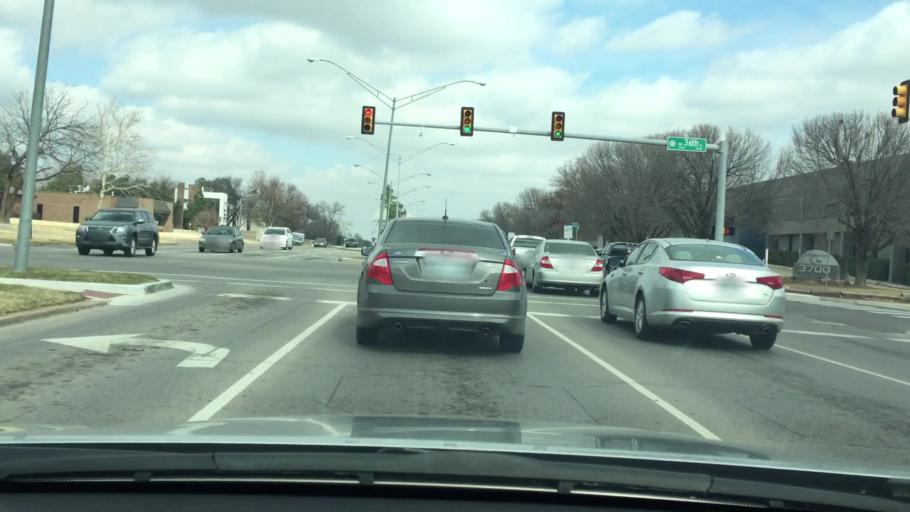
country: US
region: Oklahoma
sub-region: Oklahoma County
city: Oklahoma City
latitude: 35.5075
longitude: -97.5343
